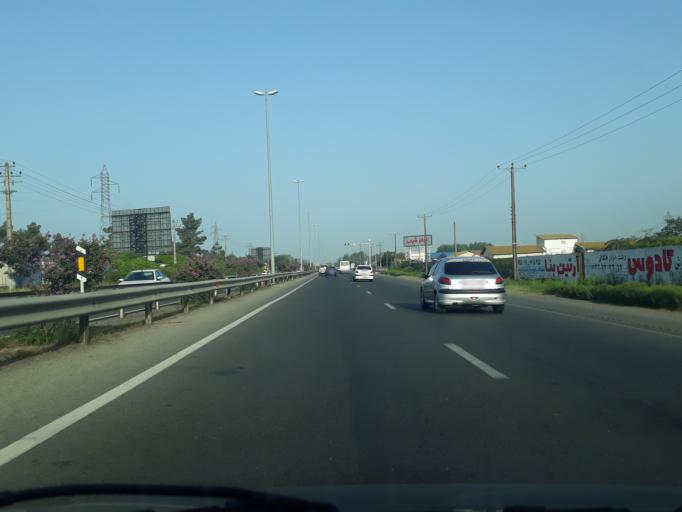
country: IR
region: Gilan
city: Bandar-e Anzali
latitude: 37.4594
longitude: 49.5946
